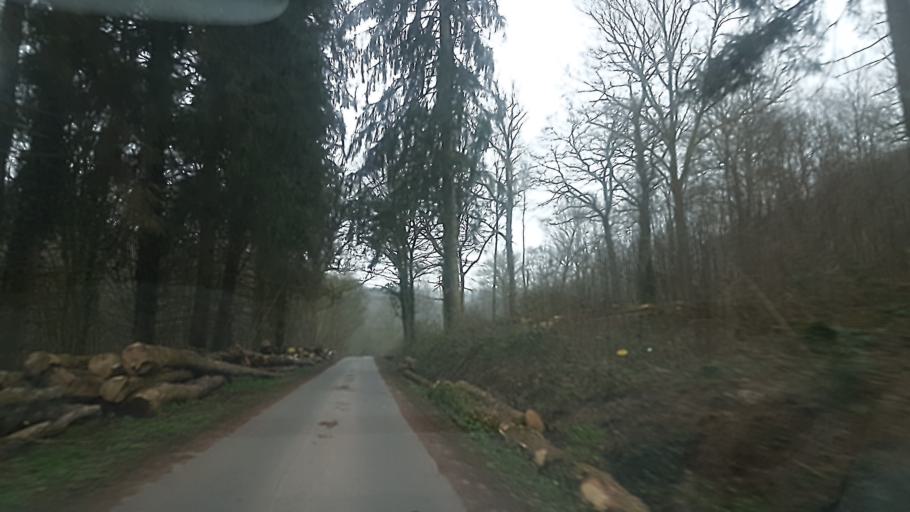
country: FR
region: Champagne-Ardenne
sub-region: Departement des Ardennes
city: Vireux-Molhain
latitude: 50.0742
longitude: 4.6530
